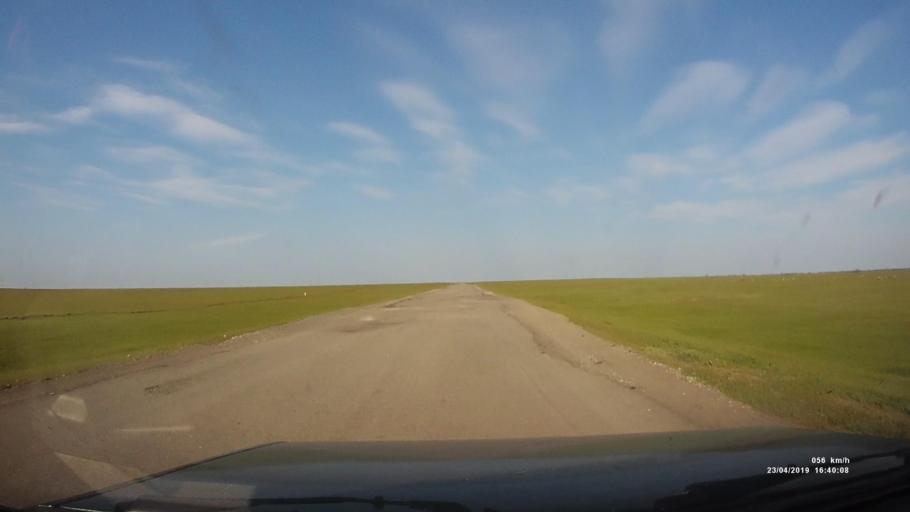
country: RU
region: Kalmykiya
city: Priyutnoye
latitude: 46.3419
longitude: 43.1737
